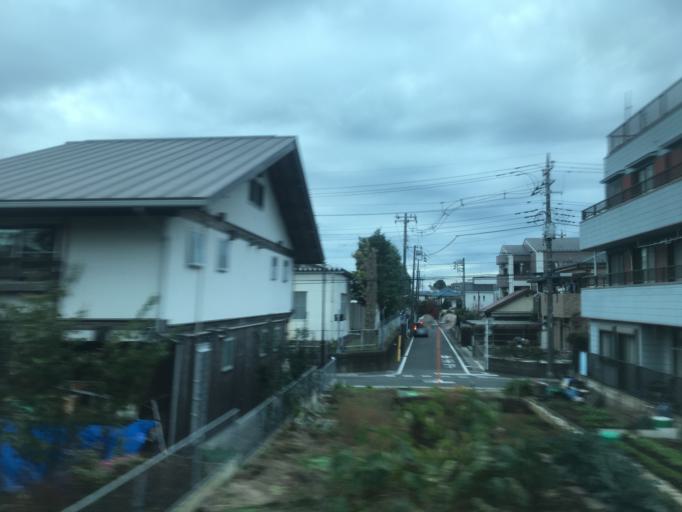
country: JP
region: Saitama
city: Ageoshimo
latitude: 35.9520
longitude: 139.6021
